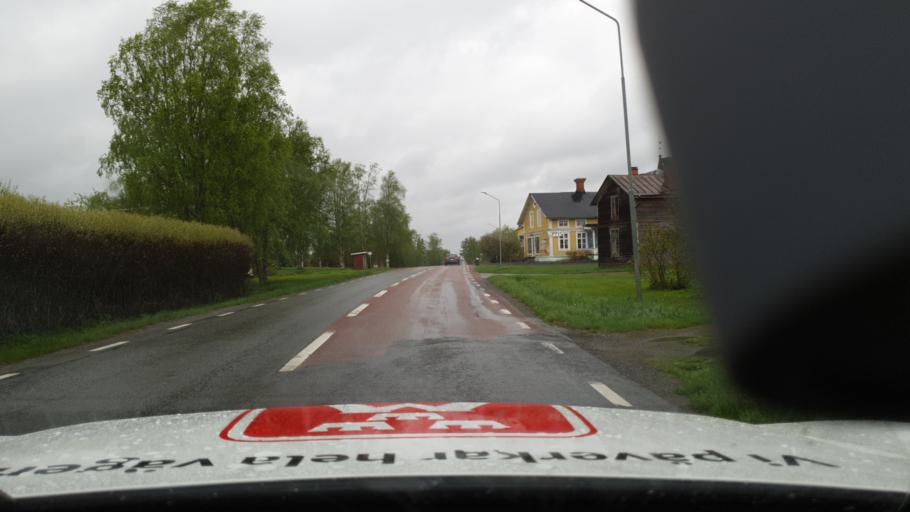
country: SE
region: Jaemtland
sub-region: Stroemsunds Kommun
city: Stroemsund
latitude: 63.7317
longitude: 15.4886
